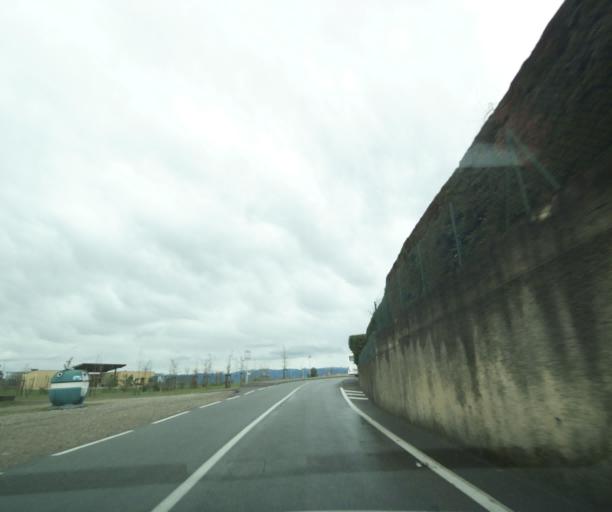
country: FR
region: Rhone-Alpes
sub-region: Departement de la Drome
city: Bourg-les-Valence
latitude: 44.9618
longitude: 4.8996
